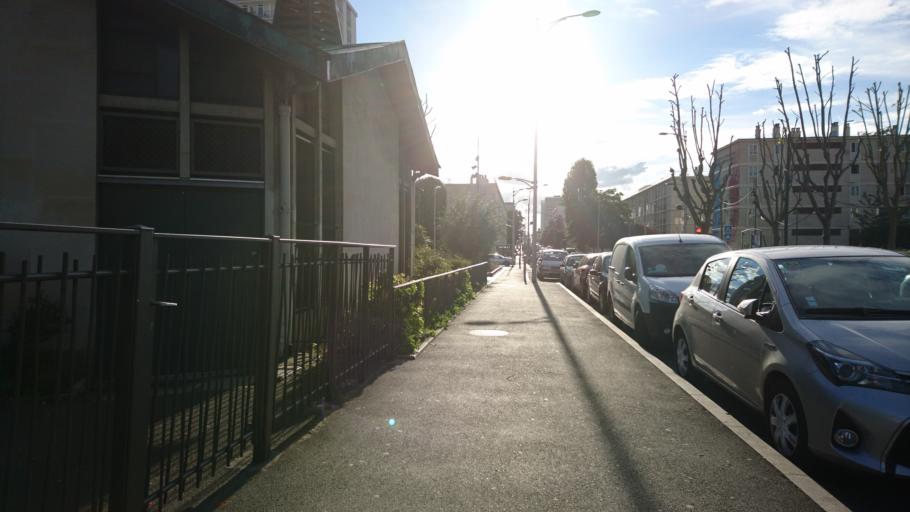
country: FR
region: Ile-de-France
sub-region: Departement du Val-d'Oise
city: Garges-les-Gonesse
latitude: 48.9756
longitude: 2.3838
